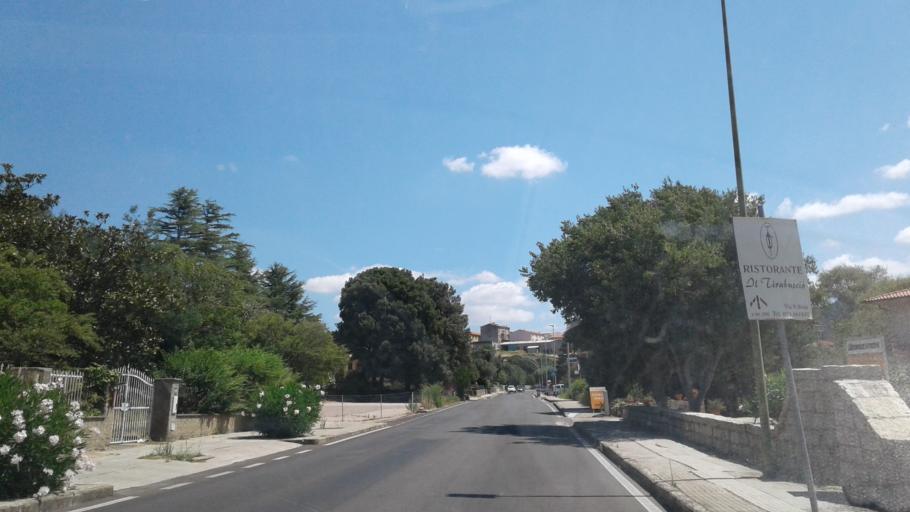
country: IT
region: Sardinia
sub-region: Provincia di Olbia-Tempio
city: Calangianus
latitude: 40.9214
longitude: 9.1845
